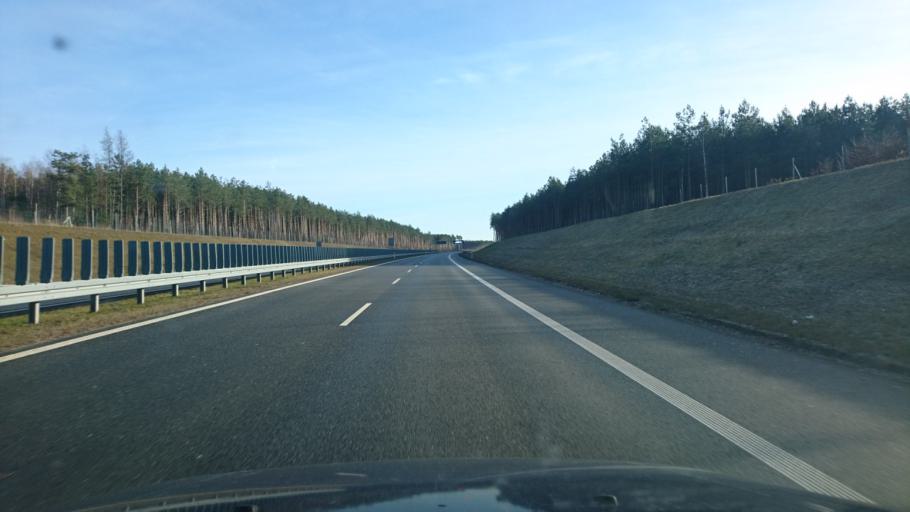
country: PL
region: Greater Poland Voivodeship
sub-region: Powiat kepinski
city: Kepno
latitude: 51.3296
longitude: 17.9770
